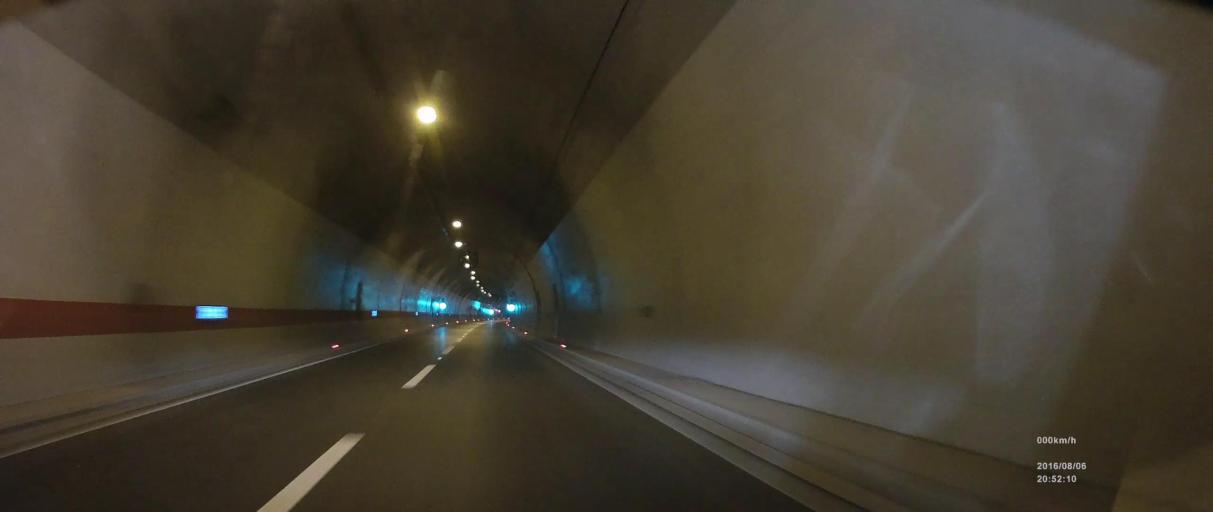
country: BA
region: Federation of Bosnia and Herzegovina
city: Ljubuski
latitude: 43.1248
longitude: 17.4851
